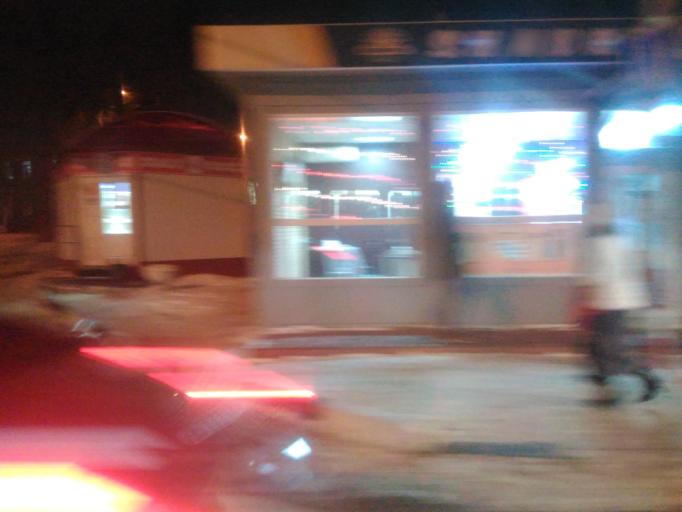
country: RU
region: Ulyanovsk
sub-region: Ulyanovskiy Rayon
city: Ulyanovsk
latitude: 54.3345
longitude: 48.3999
